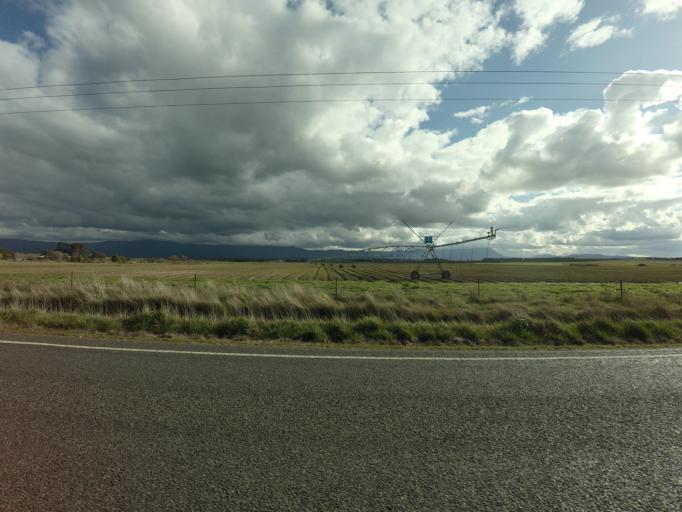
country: AU
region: Tasmania
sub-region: Northern Midlands
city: Longford
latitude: -41.7095
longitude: 147.0807
